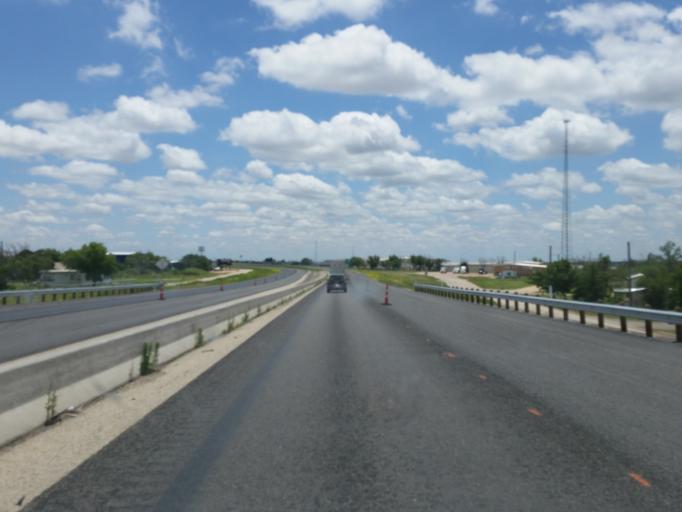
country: US
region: Texas
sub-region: Scurry County
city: Snyder
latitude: 32.7459
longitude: -100.9237
